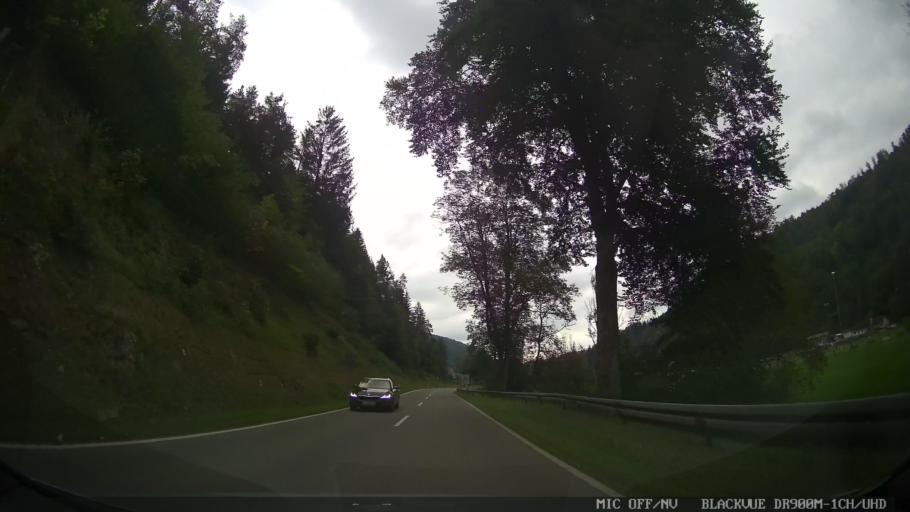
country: DE
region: Baden-Wuerttemberg
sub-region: Freiburg Region
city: Barenthal
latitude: 48.0806
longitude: 8.9252
